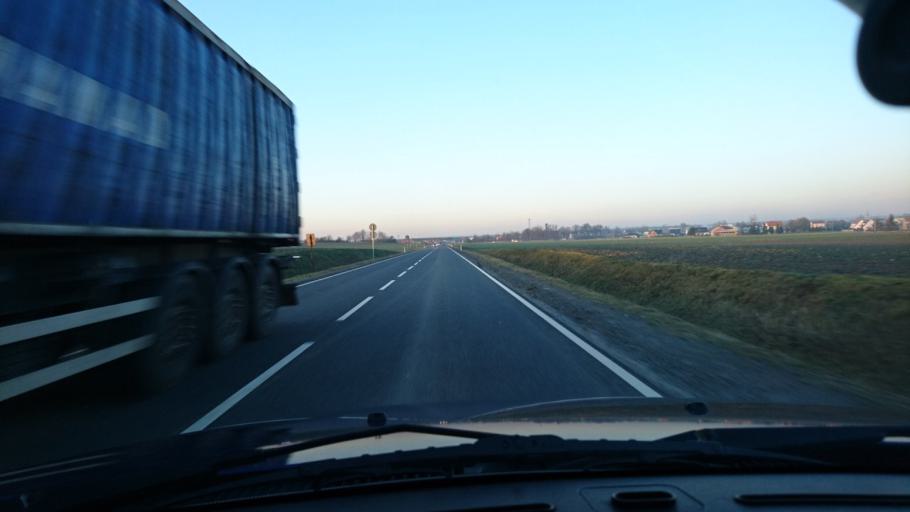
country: PL
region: Silesian Voivodeship
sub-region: Powiat gliwicki
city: Wielowies
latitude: 50.4969
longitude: 18.6067
